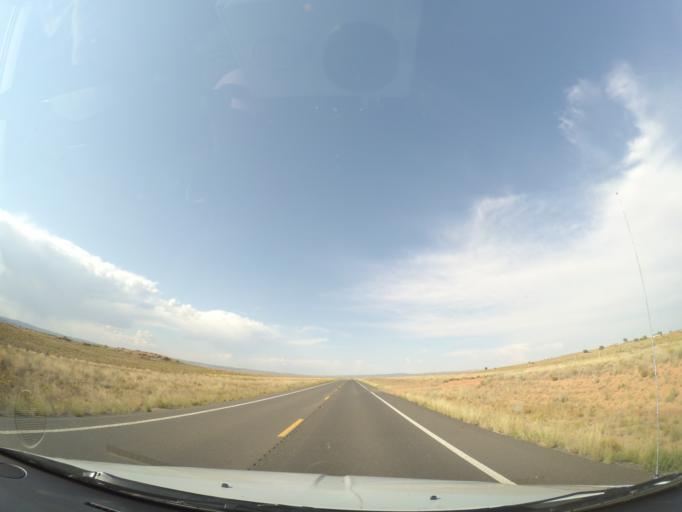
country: US
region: Arizona
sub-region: Coconino County
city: Tuba City
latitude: 36.3579
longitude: -111.4237
